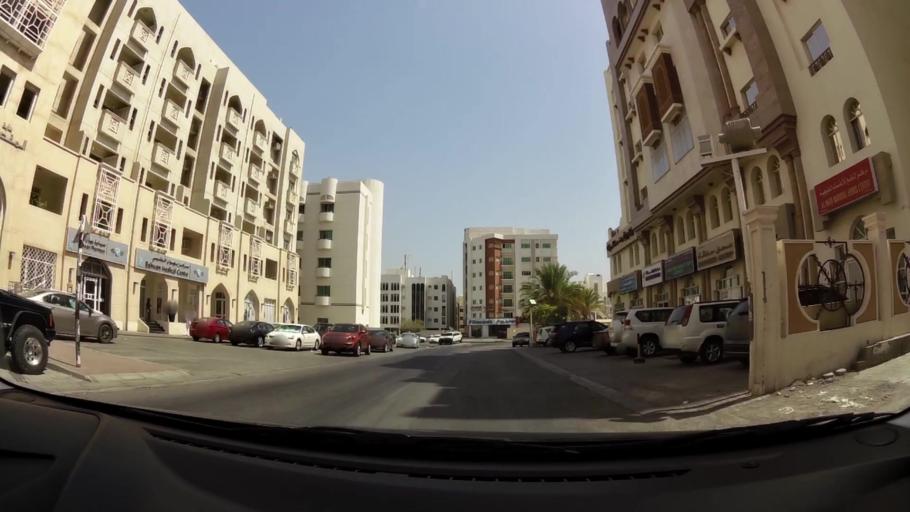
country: OM
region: Muhafazat Masqat
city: Bawshar
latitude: 23.5859
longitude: 58.4228
